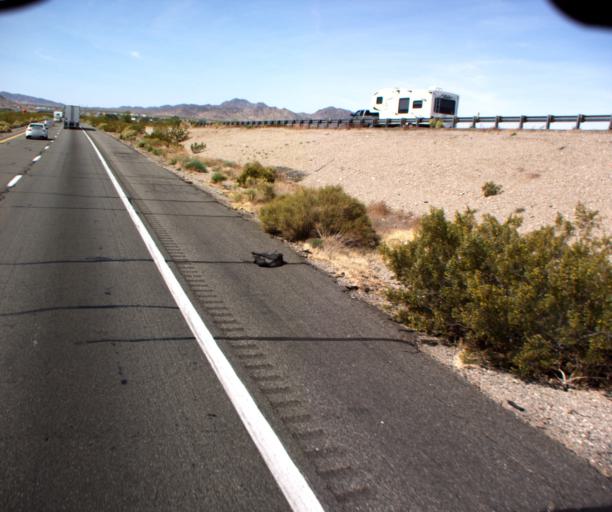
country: US
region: Arizona
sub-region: La Paz County
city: Quartzsite
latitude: 33.6655
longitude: -114.2017
